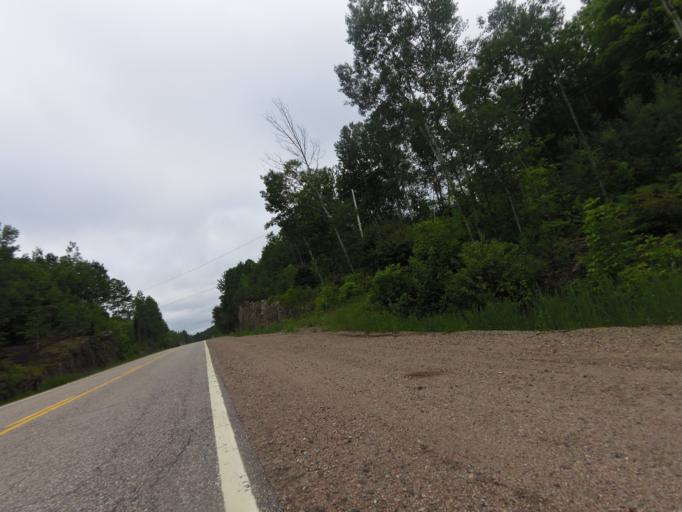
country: CA
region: Quebec
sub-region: Outaouais
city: Shawville
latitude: 45.9130
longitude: -76.3227
